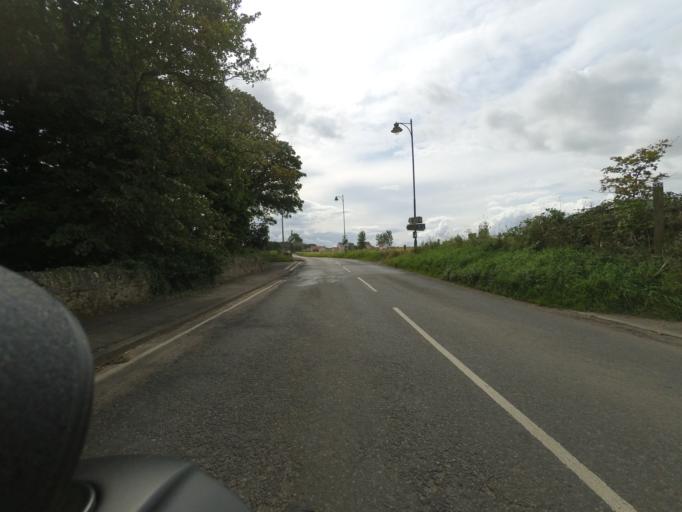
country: GB
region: Scotland
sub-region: Fife
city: Anstruther
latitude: 56.2978
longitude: -2.6589
